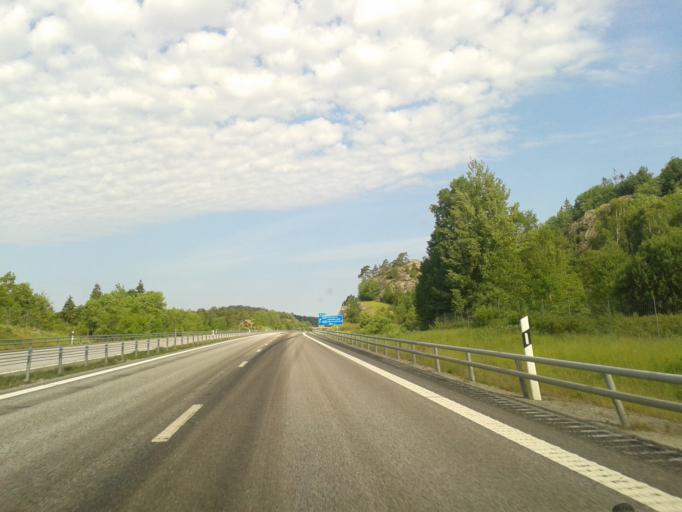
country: SE
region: Vaestra Goetaland
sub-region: Lysekils Kommun
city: Brastad
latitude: 58.5556
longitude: 11.4963
